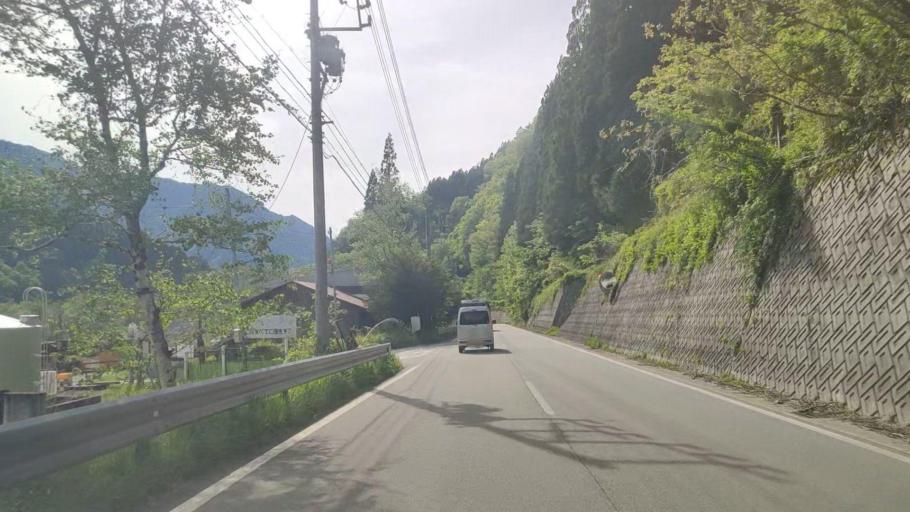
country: JP
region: Gifu
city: Takayama
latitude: 36.2600
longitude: 137.4542
